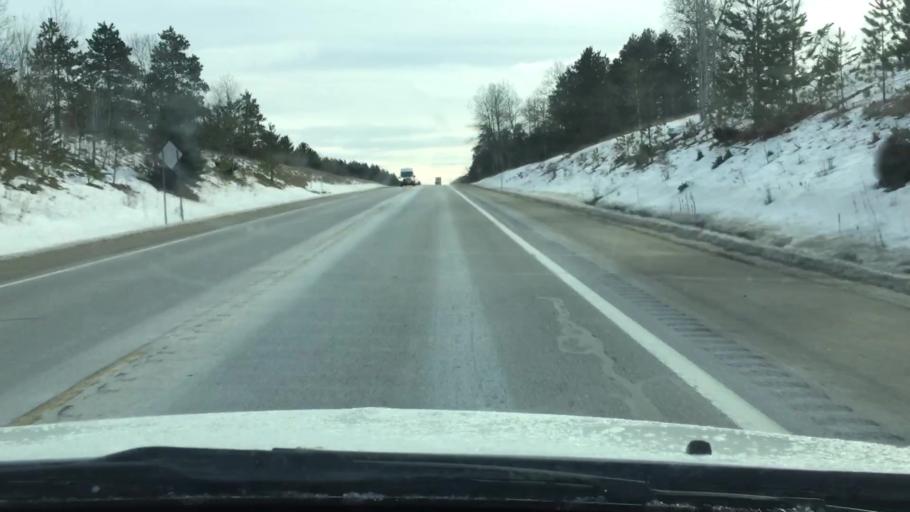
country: US
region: Michigan
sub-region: Wexford County
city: Manton
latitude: 44.4825
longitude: -85.4064
